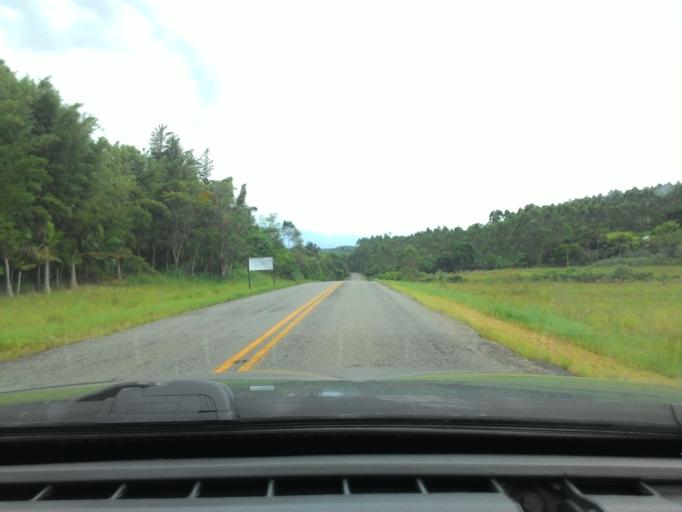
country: BR
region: Sao Paulo
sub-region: Pariquera-Acu
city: Pariquera Acu
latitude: -24.7489
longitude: -47.7962
